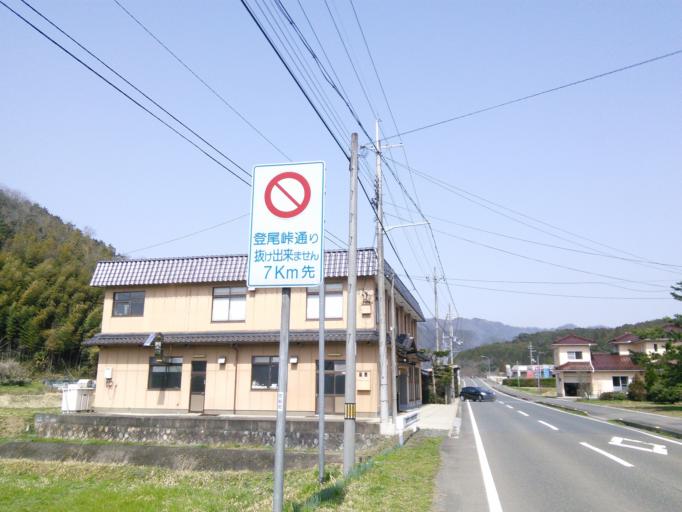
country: JP
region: Kyoto
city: Ayabe
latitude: 35.3714
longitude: 135.2402
